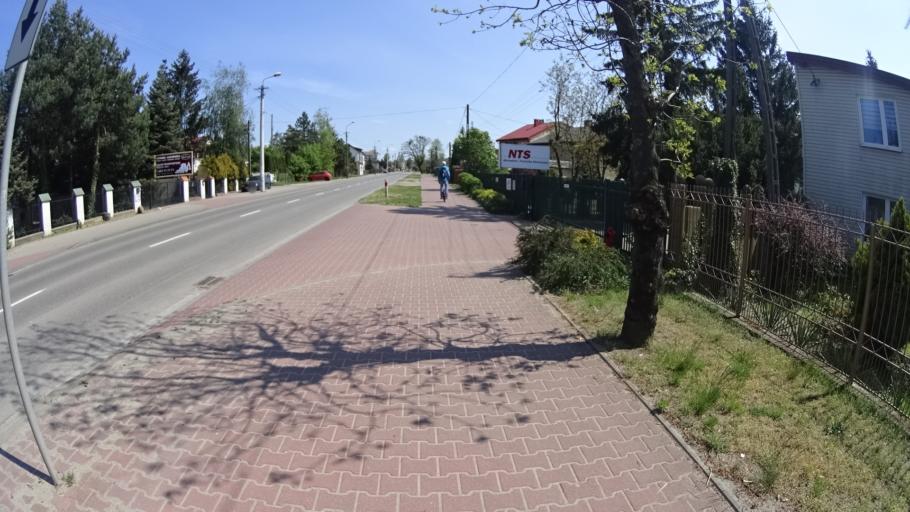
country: PL
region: Masovian Voivodeship
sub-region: Powiat warszawski zachodni
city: Jozefow
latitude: 52.2535
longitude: 20.7299
